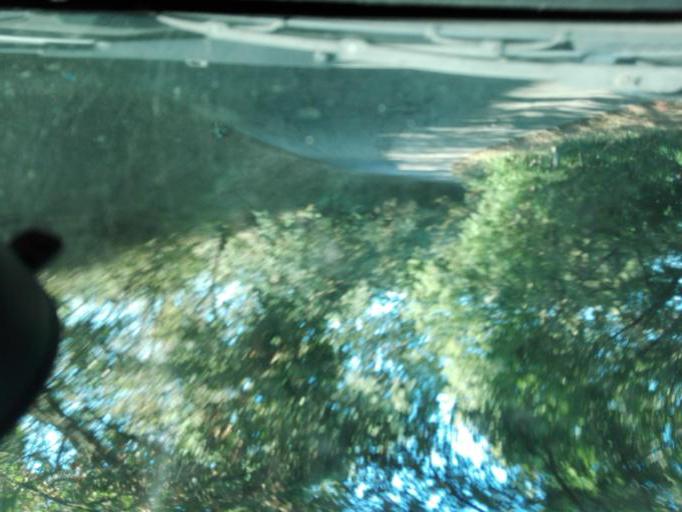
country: IT
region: Abruzzo
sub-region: Provincia di Pescara
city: Cappelle sul Tavo
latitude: 42.4505
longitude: 14.0884
